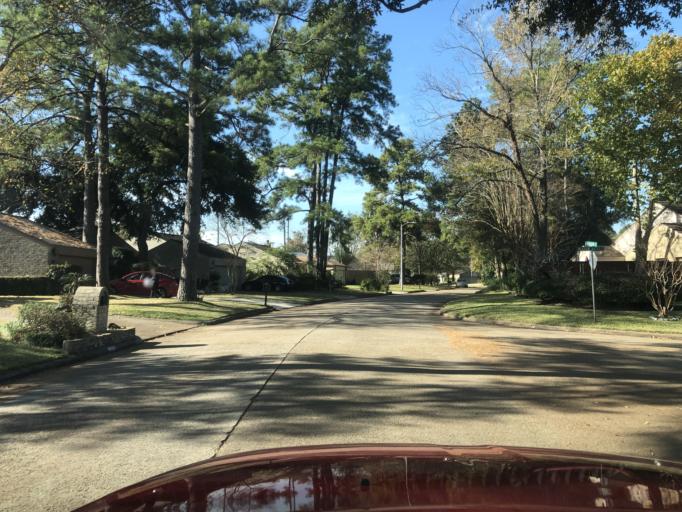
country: US
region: Texas
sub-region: Harris County
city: Spring
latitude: 30.0136
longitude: -95.4585
